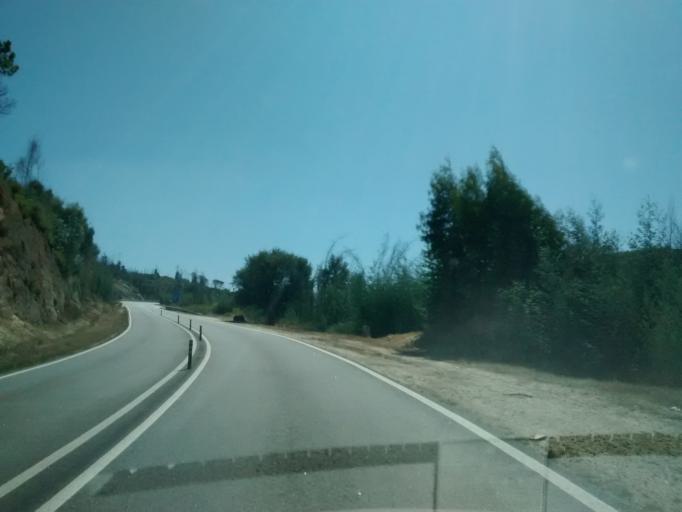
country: PT
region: Coimbra
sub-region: Tabua
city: Tabua
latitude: 40.3688
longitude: -8.0597
